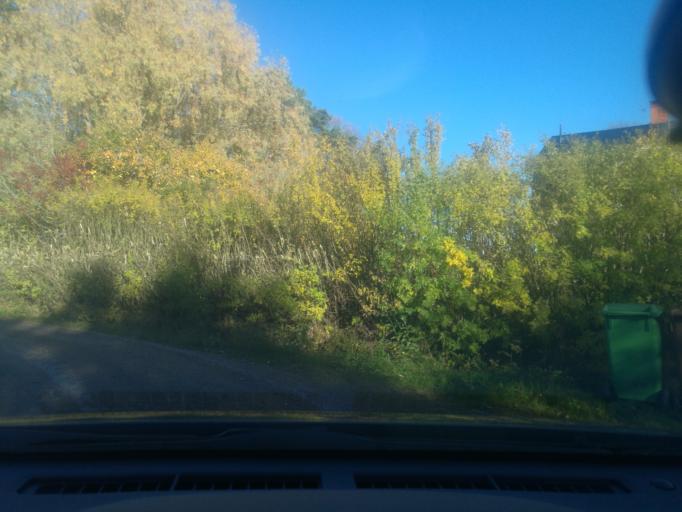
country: SE
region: Vaestmanland
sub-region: Kopings Kommun
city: Koping
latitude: 59.5938
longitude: 16.0068
